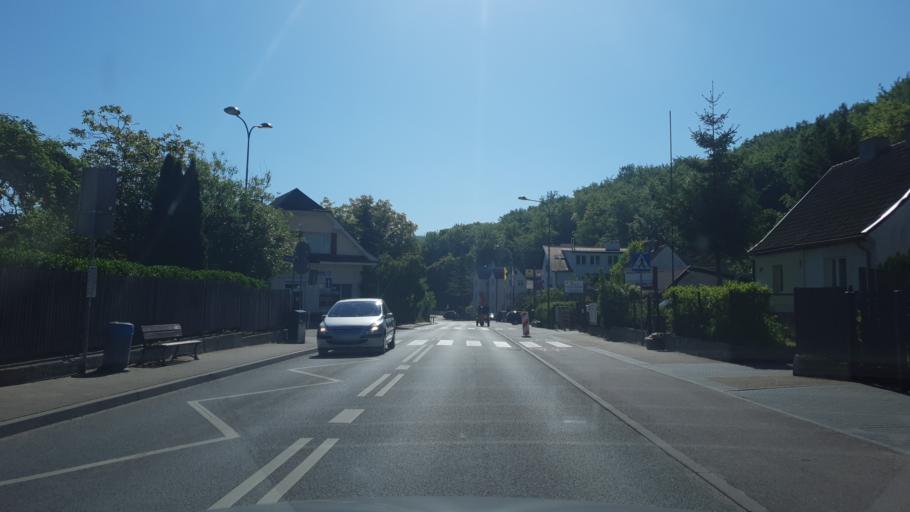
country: PL
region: Pomeranian Voivodeship
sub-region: Sopot
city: Sopot
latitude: 54.4557
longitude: 18.5432
